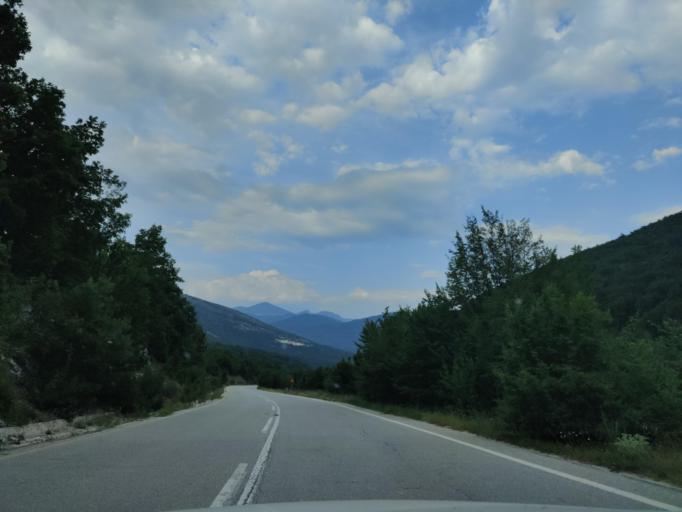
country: GR
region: East Macedonia and Thrace
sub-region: Nomos Dramas
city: Volakas
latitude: 41.2919
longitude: 23.9439
